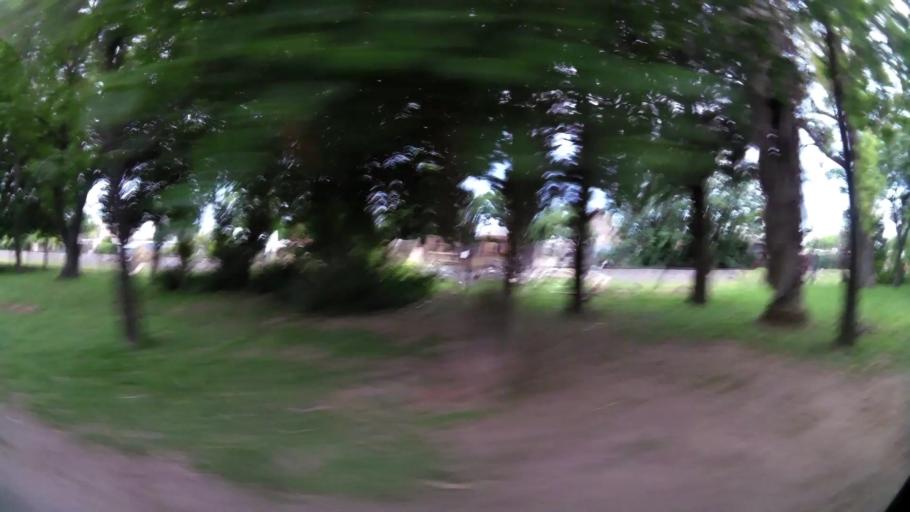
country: AR
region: Santa Fe
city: Granadero Baigorria
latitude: -32.8797
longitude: -60.7039
